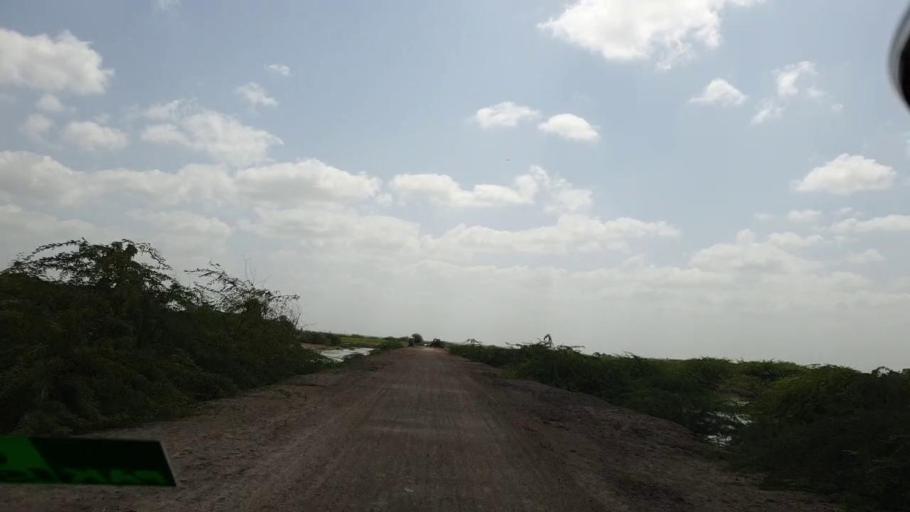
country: PK
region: Sindh
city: Kadhan
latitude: 24.5917
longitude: 69.1831
